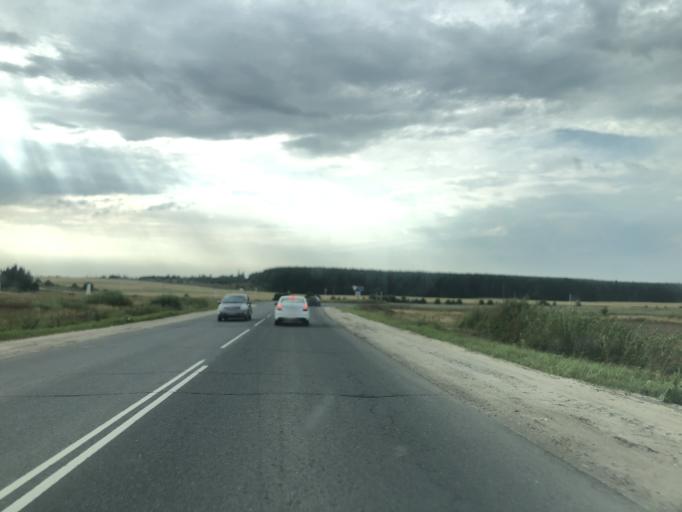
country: RU
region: Ivanovo
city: Shuya
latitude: 56.8608
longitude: 41.4562
